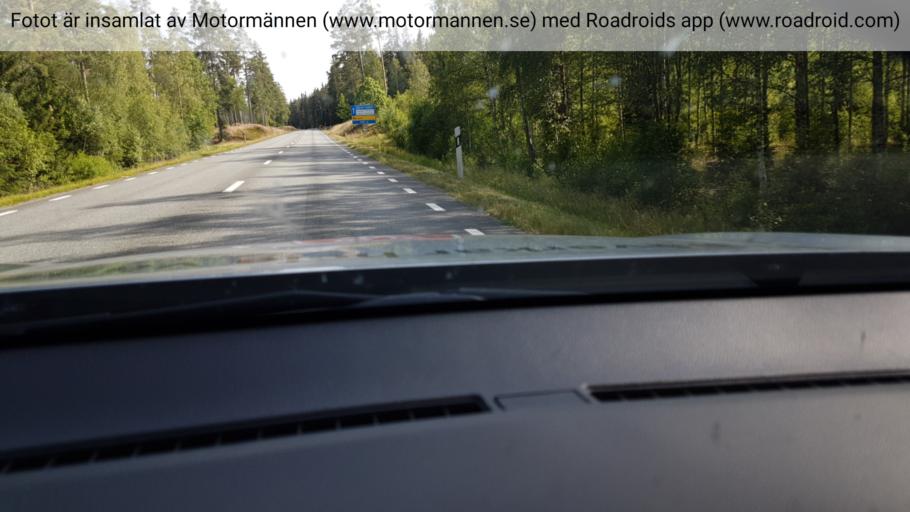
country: SE
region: Joenkoeping
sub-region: Eksjo Kommun
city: Eksjoe
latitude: 57.5935
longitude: 14.9694
